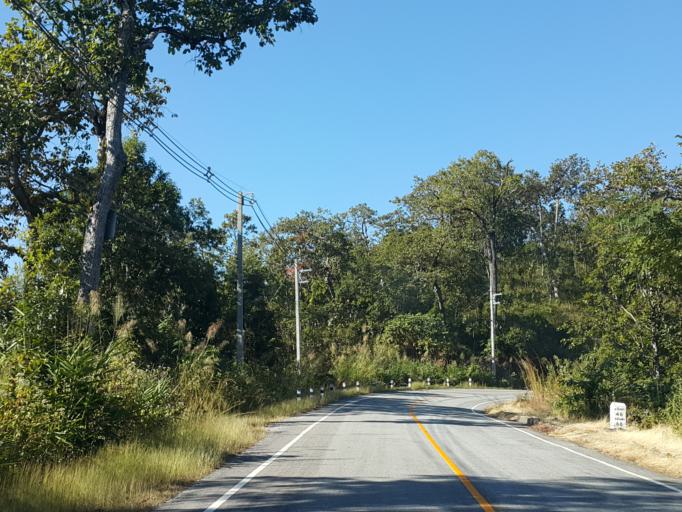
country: TH
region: Chiang Mai
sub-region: Amphoe Chiang Dao
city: Chiang Dao
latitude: 19.5279
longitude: 98.8902
